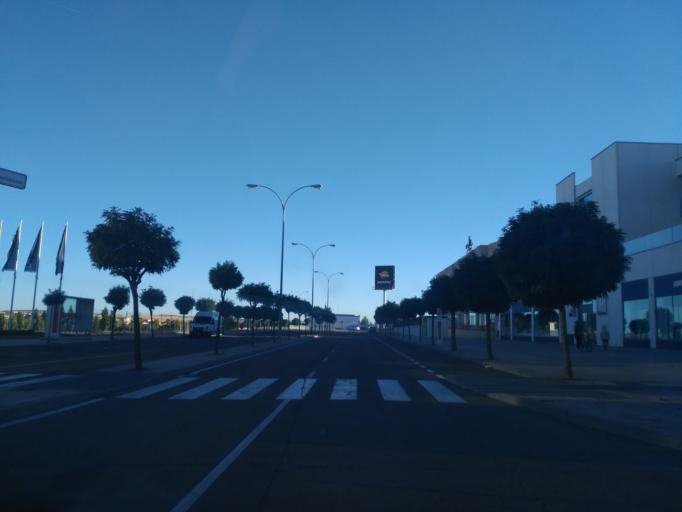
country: ES
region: Castille and Leon
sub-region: Provincia de Salamanca
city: Carbajosa de la Sagrada
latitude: 40.9412
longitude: -5.6553
